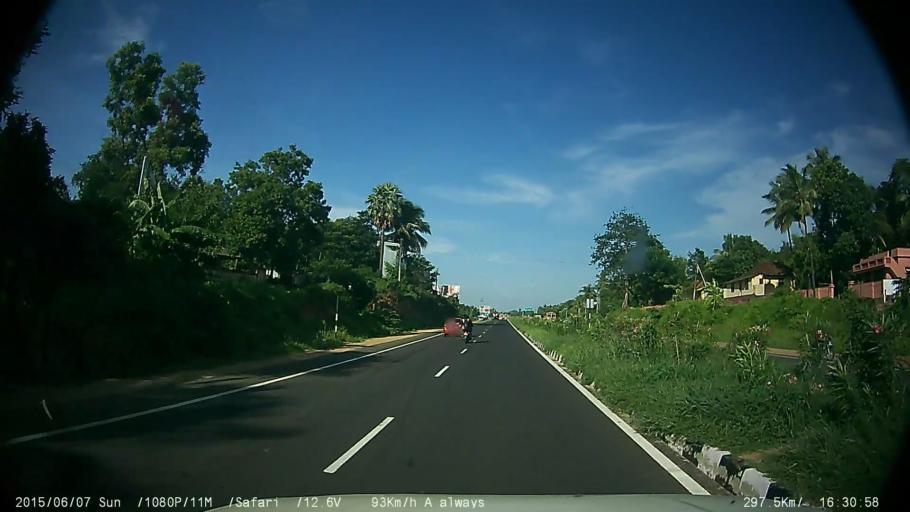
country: IN
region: Kerala
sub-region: Palakkad district
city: Palakkad
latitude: 10.7388
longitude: 76.6395
